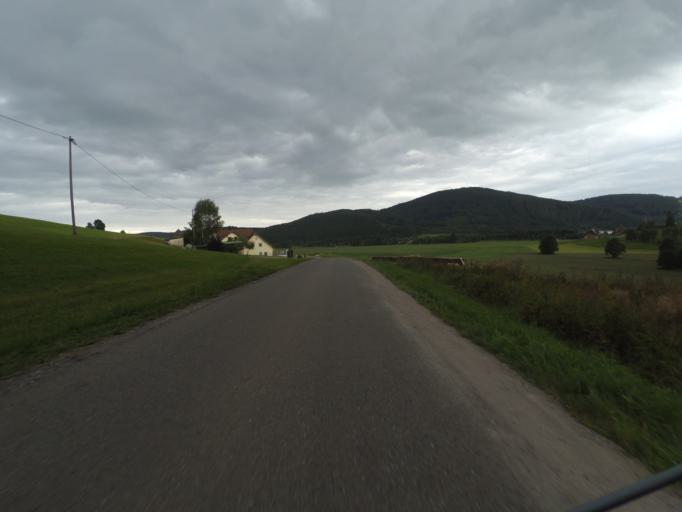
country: DE
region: Baden-Wuerttemberg
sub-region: Freiburg Region
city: Titisee-Neustadt
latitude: 47.9194
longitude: 8.1629
